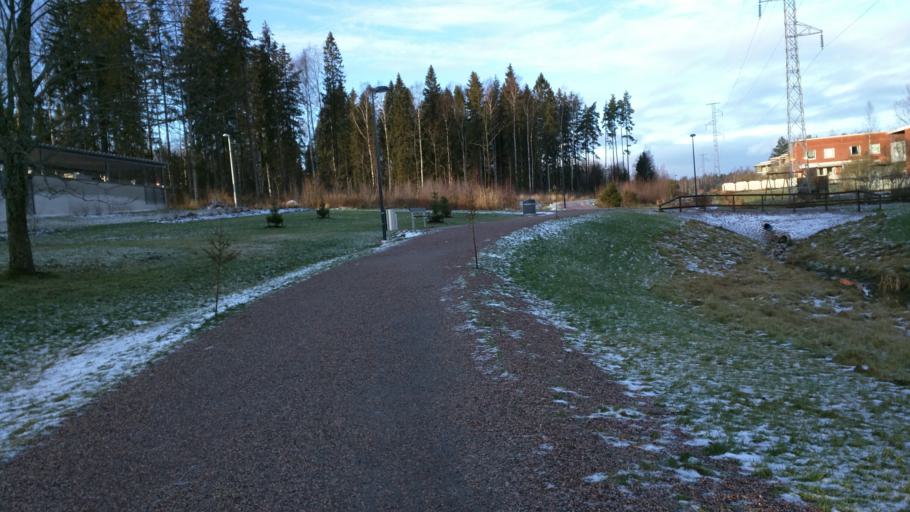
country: FI
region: Uusimaa
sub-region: Helsinki
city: Kilo
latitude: 60.2556
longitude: 24.7982
